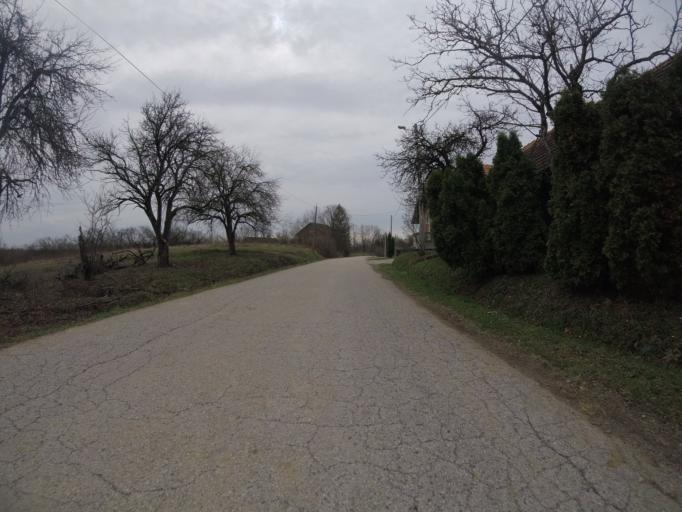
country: HR
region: Zagrebacka
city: Lukavec
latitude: 45.5790
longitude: 15.9644
